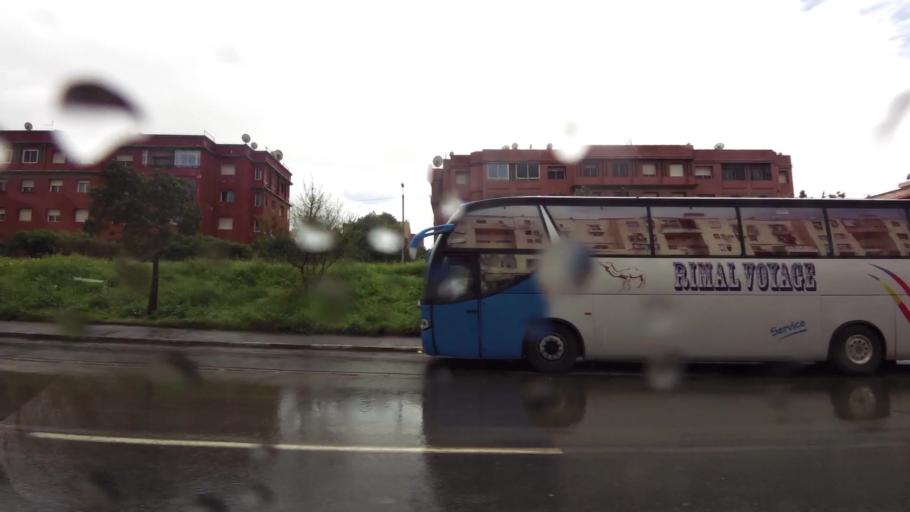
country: MA
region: Grand Casablanca
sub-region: Casablanca
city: Casablanca
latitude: 33.5324
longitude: -7.6497
